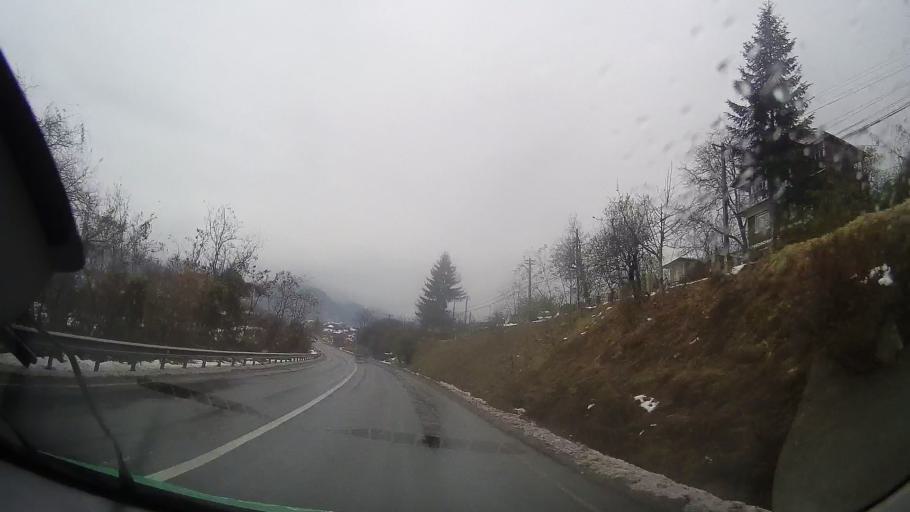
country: RO
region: Neamt
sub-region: Comuna Alexandru Cel Bun
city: Vadurele
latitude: 46.9404
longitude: 26.2671
